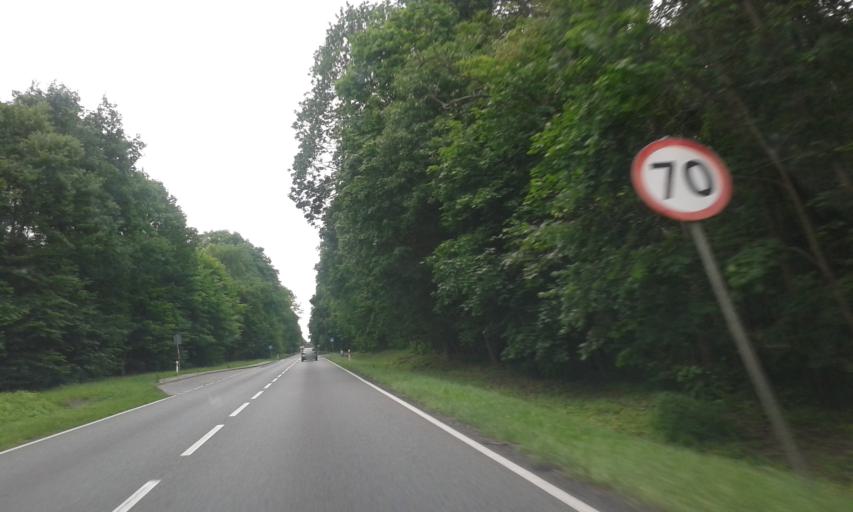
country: PL
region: Kujawsko-Pomorskie
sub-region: Powiat bydgoski
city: Biale Blota
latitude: 53.1820
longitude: 17.9370
